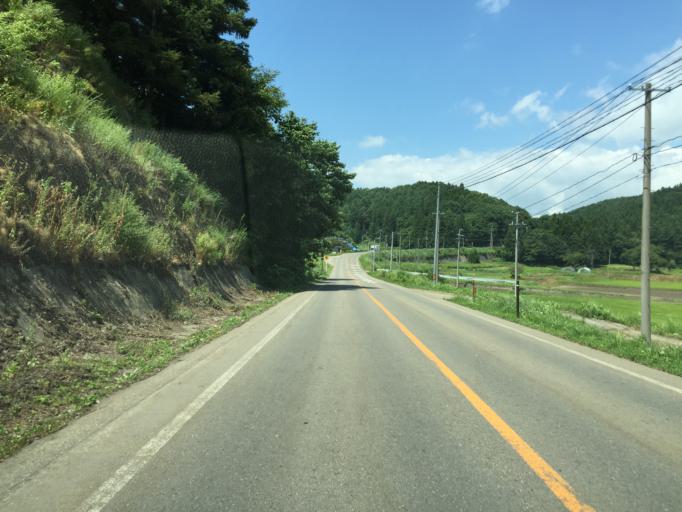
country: JP
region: Fukushima
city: Inawashiro
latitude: 37.5013
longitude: 139.9959
